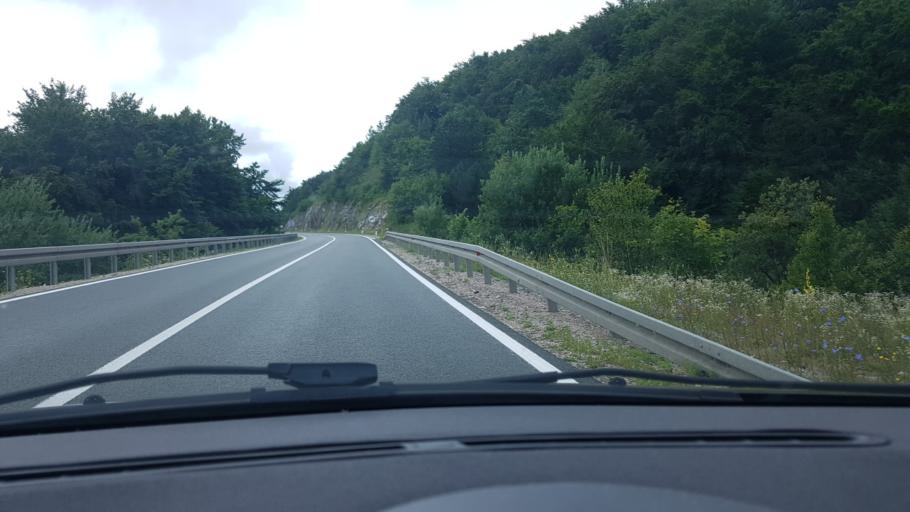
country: BA
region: Federation of Bosnia and Herzegovina
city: Izacic
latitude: 44.8661
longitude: 15.7017
